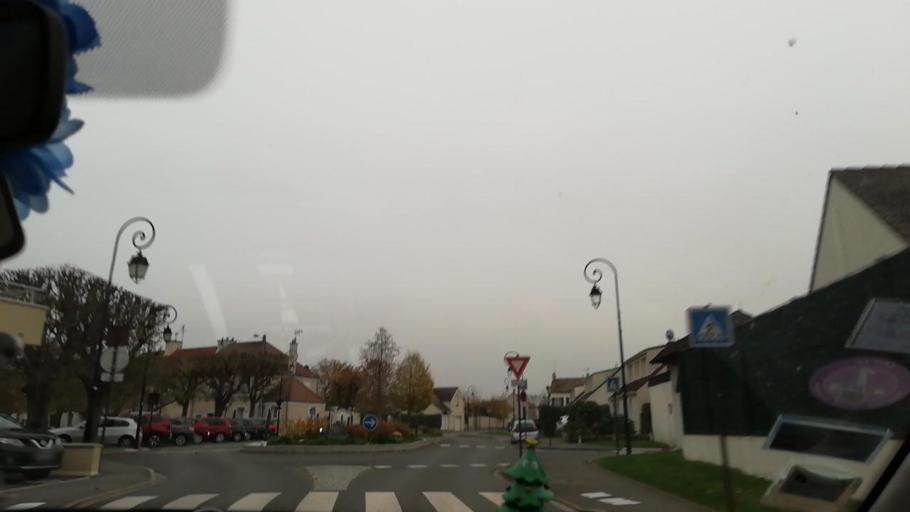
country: FR
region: Ile-de-France
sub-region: Departement de Seine-et-Marne
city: Claye-Souilly
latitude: 48.9497
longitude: 2.6756
